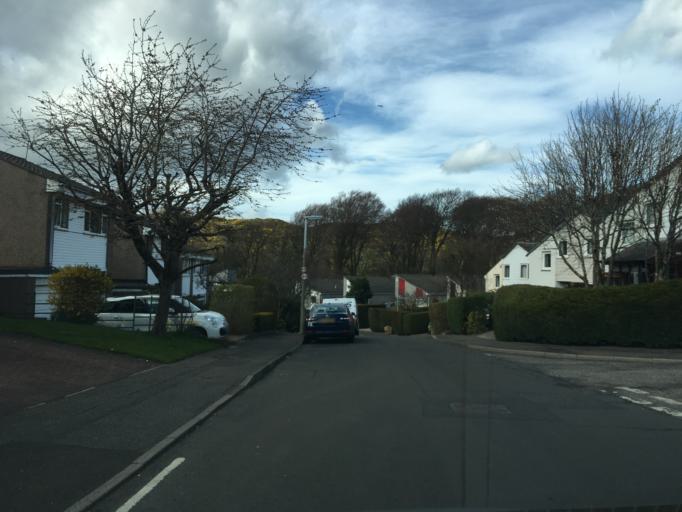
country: GB
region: Scotland
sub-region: Edinburgh
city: Edinburgh
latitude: 55.9082
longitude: -3.1991
